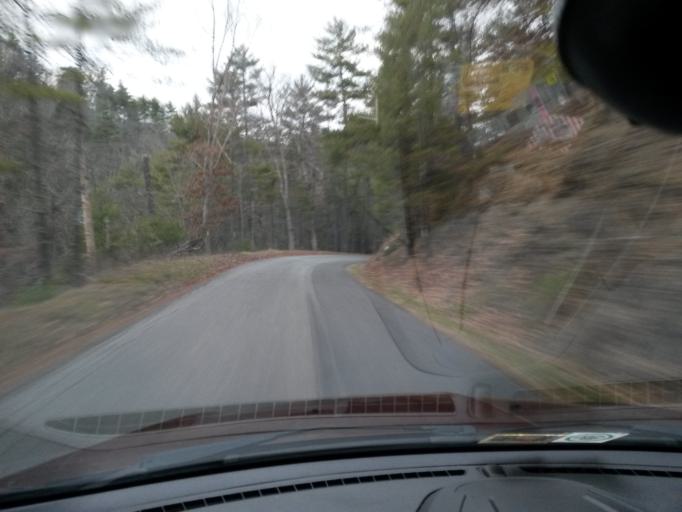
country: US
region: Virginia
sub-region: Bath County
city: Warm Springs
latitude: 37.9979
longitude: -79.7097
